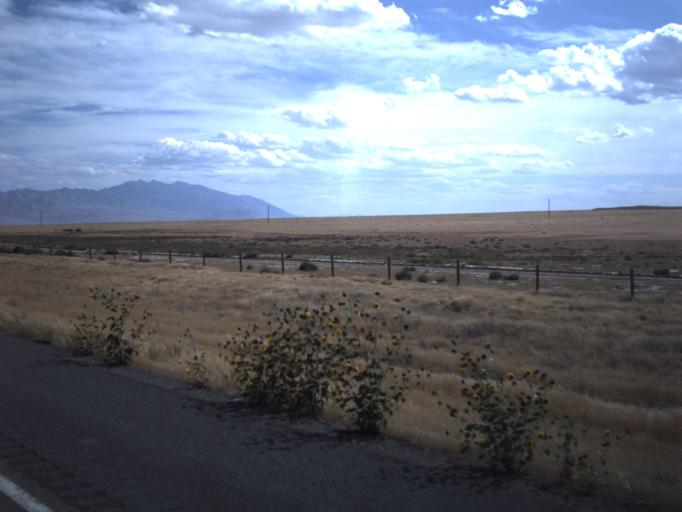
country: US
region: Utah
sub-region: Tooele County
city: Grantsville
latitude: 40.8032
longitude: -112.8555
